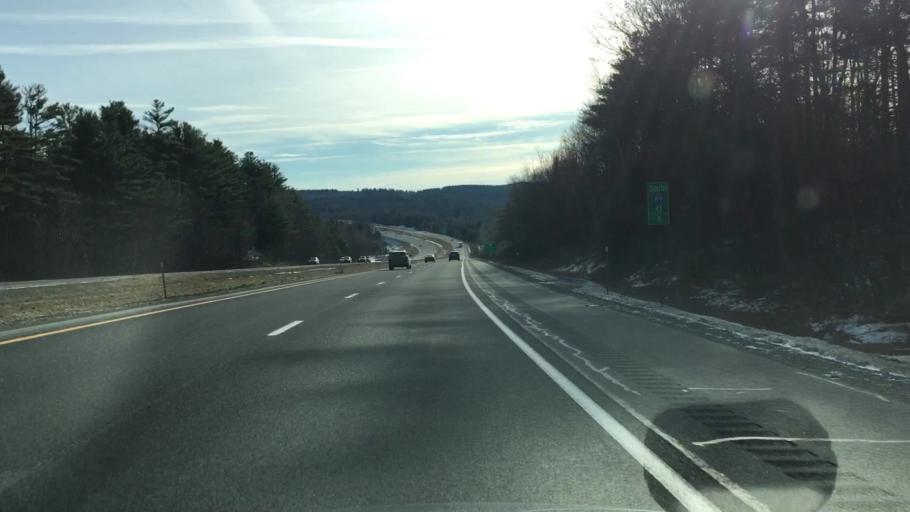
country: US
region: New Hampshire
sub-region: Sullivan County
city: Grantham
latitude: 43.5102
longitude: -72.1346
